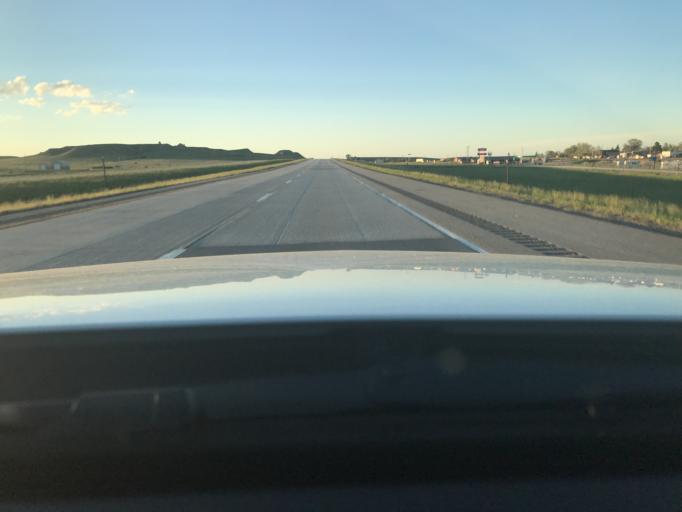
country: US
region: Wyoming
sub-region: Platte County
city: Guernsey
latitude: 42.4990
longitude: -105.0310
